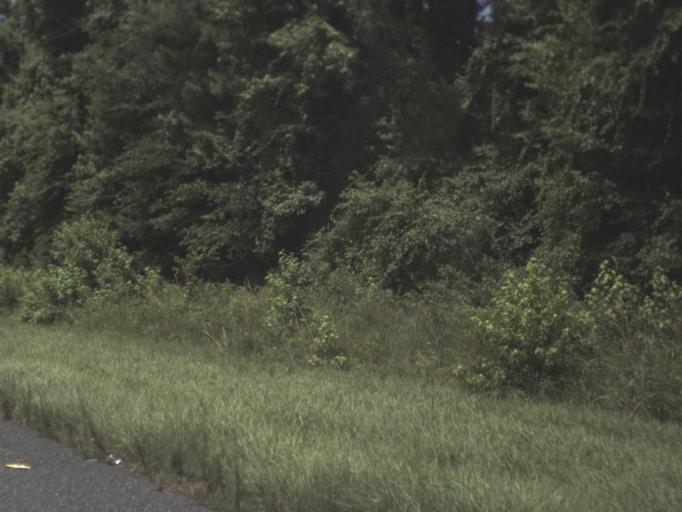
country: US
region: Florida
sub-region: Taylor County
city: Perry
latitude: 30.2959
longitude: -83.7413
